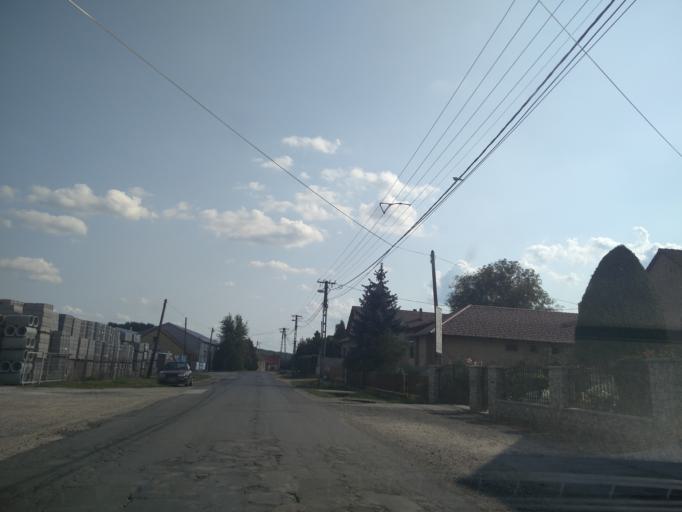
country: HU
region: Zala
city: Zalaegerszeg
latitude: 46.8822
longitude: 16.7519
